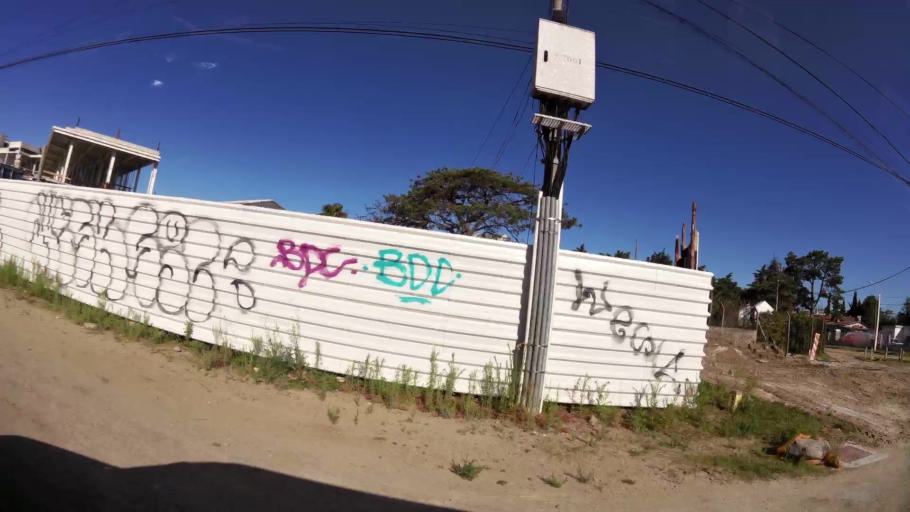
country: UY
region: Canelones
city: Barra de Carrasco
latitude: -34.8704
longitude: -56.0316
